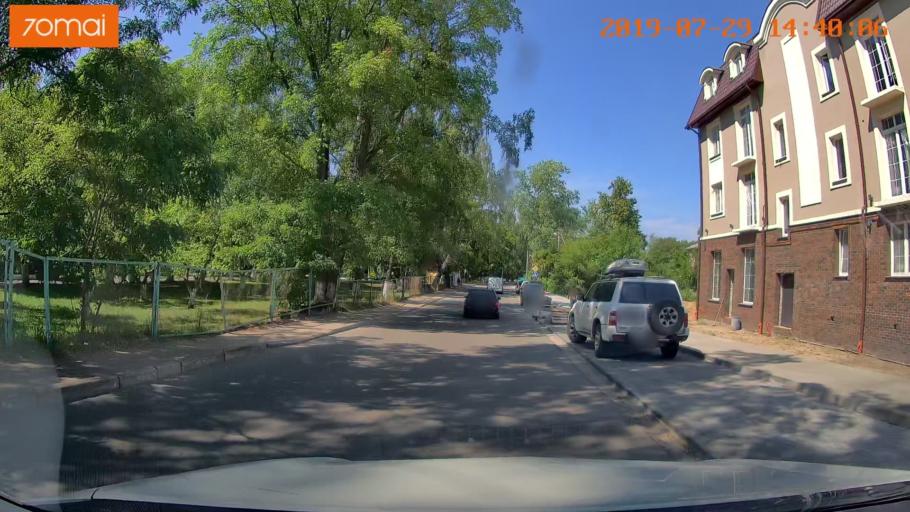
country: RU
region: Kaliningrad
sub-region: Gorod Kaliningrad
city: Baltiysk
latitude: 54.6535
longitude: 19.9023
